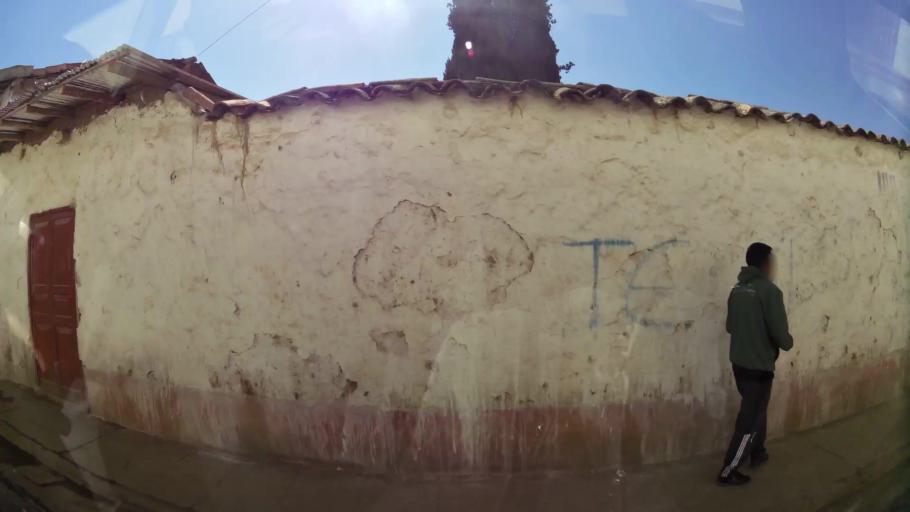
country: PE
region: Junin
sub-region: Provincia de Concepcion
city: Concepcion
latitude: -11.9190
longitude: -75.3122
